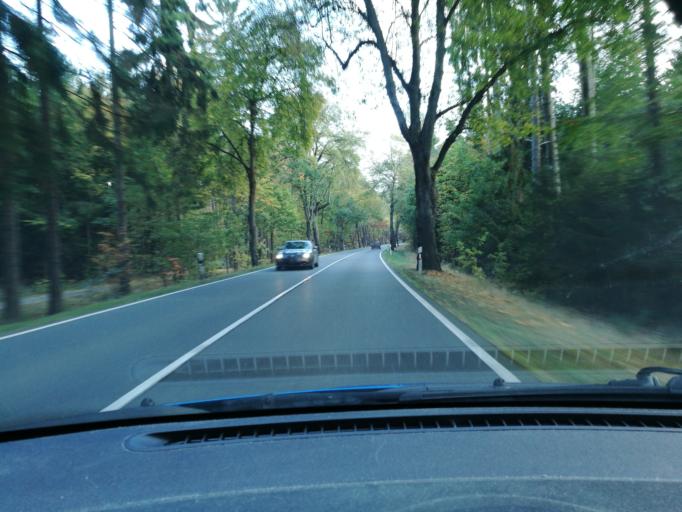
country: DE
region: Lower Saxony
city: Karwitz
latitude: 53.1155
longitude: 11.0042
